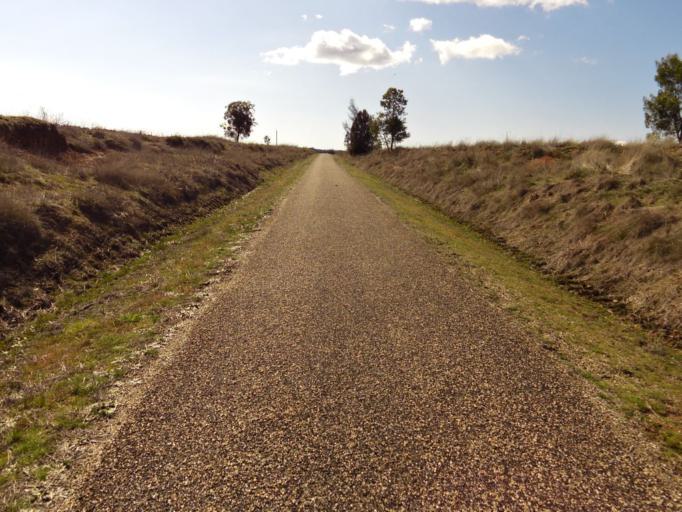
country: AU
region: Victoria
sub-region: Wangaratta
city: Wangaratta
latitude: -36.3982
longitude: 146.6502
